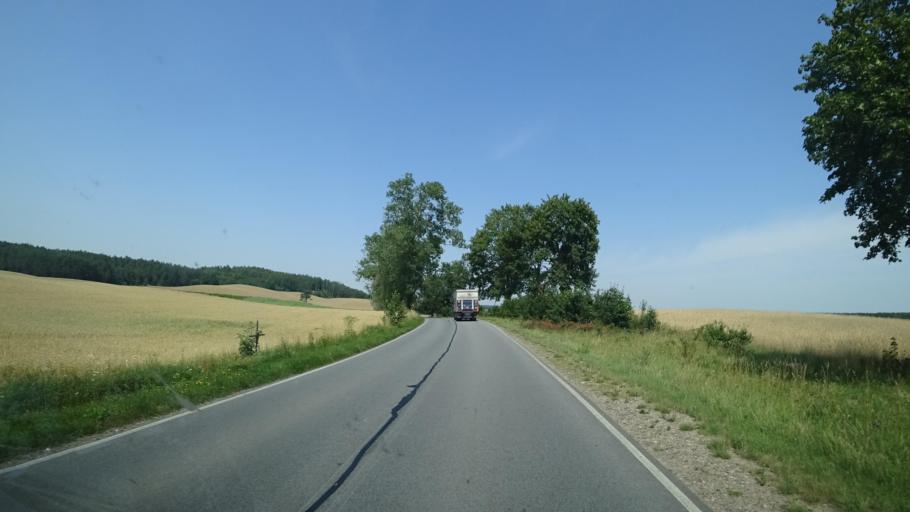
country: PL
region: Pomeranian Voivodeship
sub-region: Powiat koscierski
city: Lipusz
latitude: 54.0694
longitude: 17.8046
